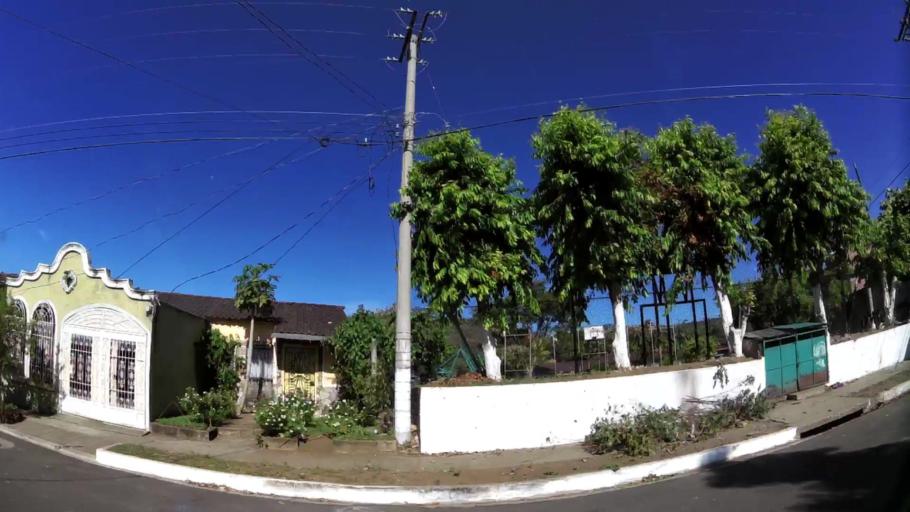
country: SV
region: Sonsonate
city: Sonzacate
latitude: 13.7395
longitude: -89.7175
